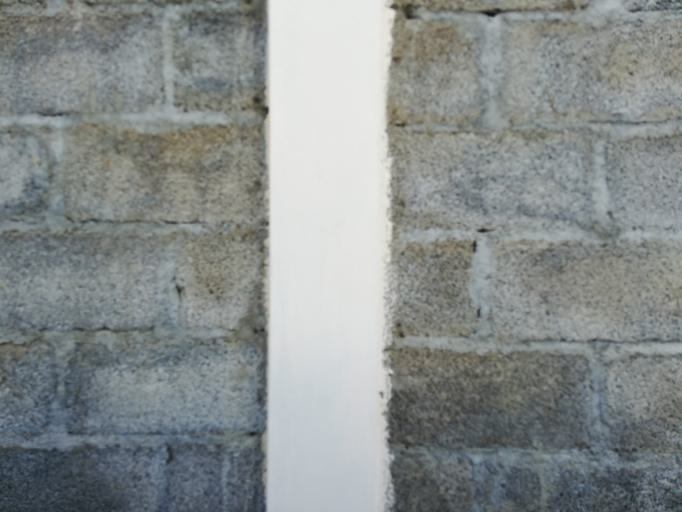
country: MU
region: Port Louis
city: Port Louis
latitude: -20.1651
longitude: 57.4818
